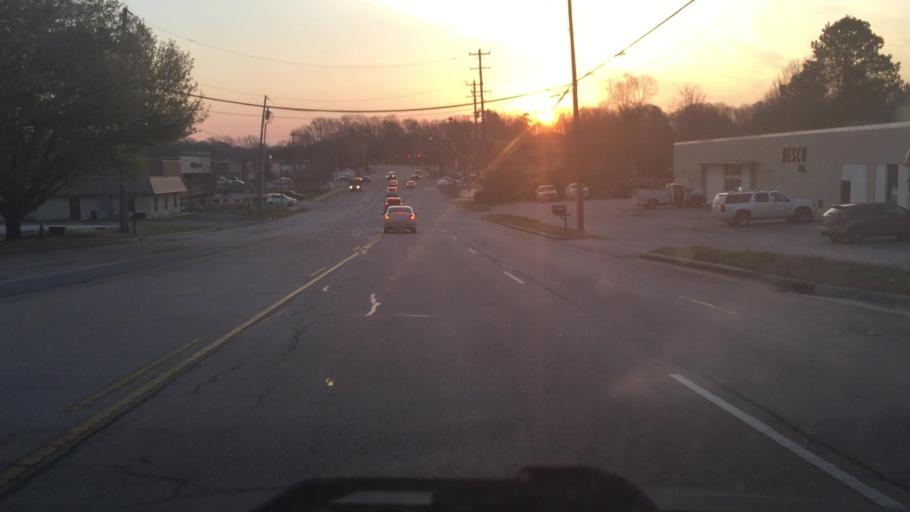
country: US
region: North Carolina
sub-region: Rowan County
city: Salisbury
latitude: 35.6643
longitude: -80.5017
